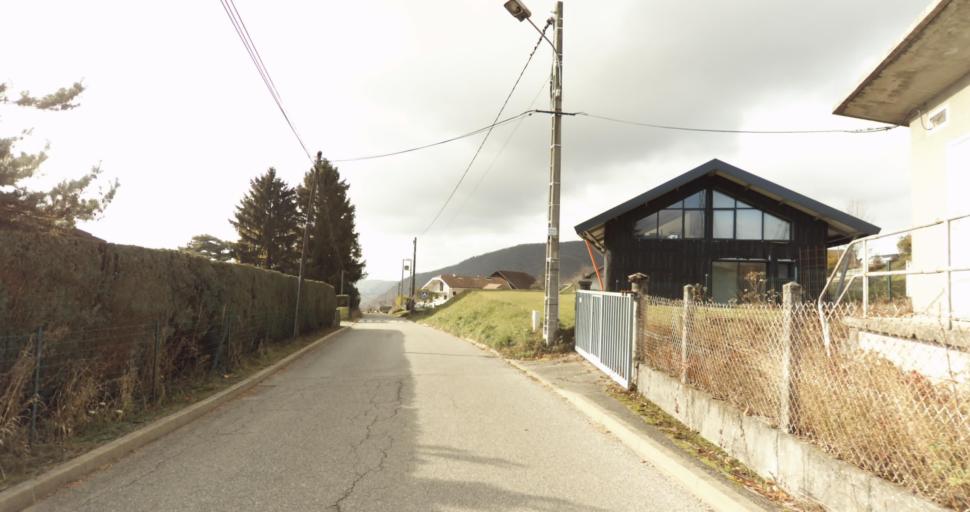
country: FR
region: Rhone-Alpes
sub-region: Departement de la Haute-Savoie
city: Epagny
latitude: 45.9603
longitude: 6.0793
